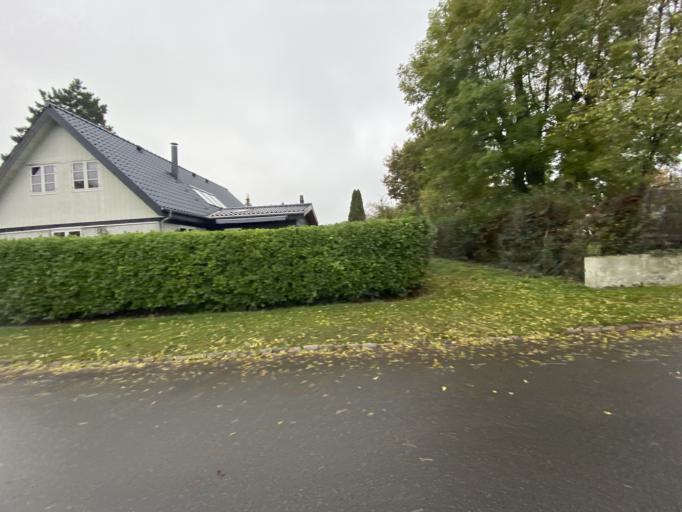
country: DK
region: Capital Region
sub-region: Dragor Kommune
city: Dragor
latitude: 55.5707
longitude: 12.6216
